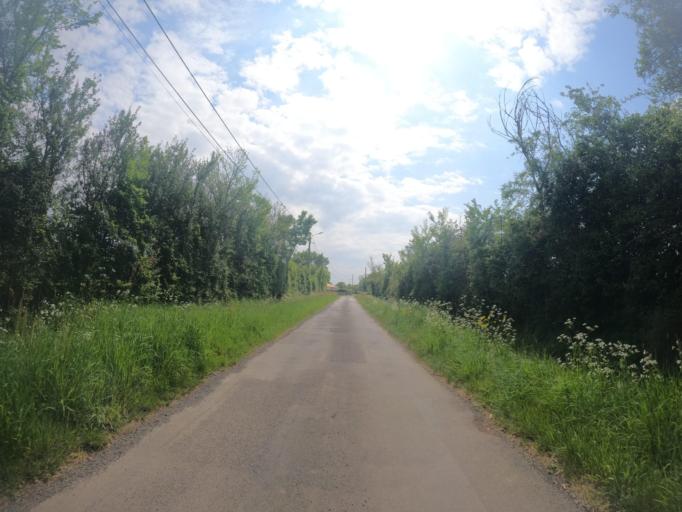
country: FR
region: Poitou-Charentes
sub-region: Departement des Deux-Sevres
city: Saint-Varent
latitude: 46.8973
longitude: -0.2913
